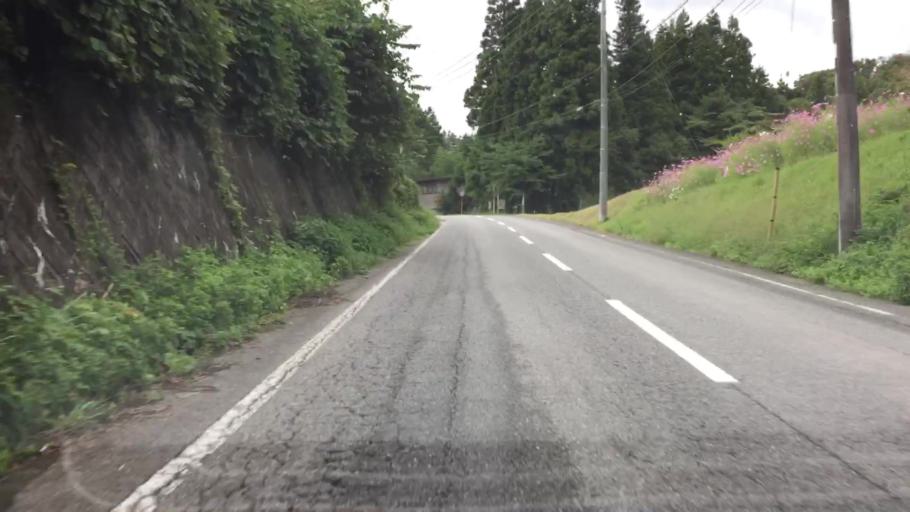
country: JP
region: Tochigi
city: Nikko
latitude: 36.7595
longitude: 139.6620
